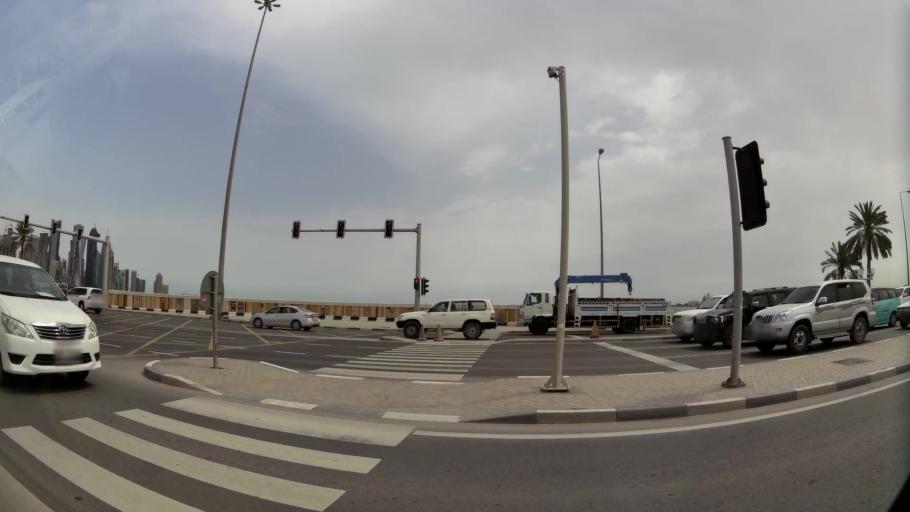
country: QA
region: Baladiyat ad Dawhah
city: Doha
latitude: 25.3040
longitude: 51.5177
